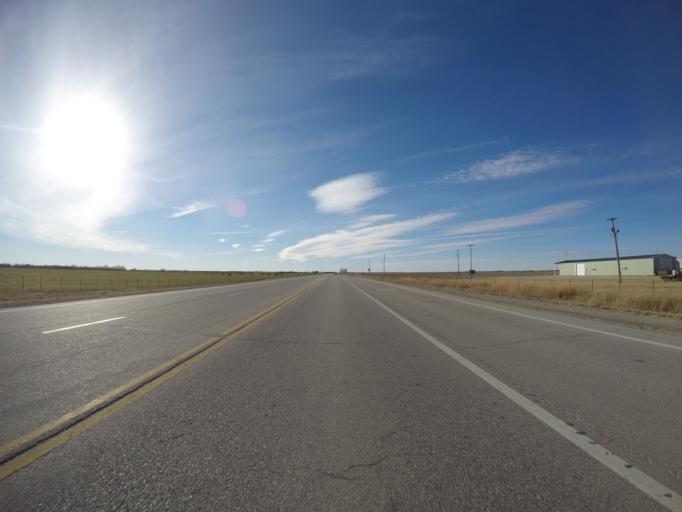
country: US
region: Kansas
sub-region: McPherson County
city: Moundridge
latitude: 38.3769
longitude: -97.4308
